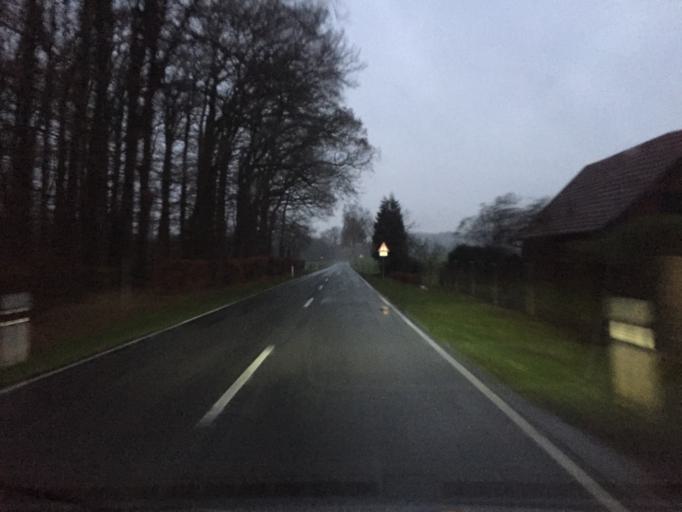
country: DE
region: Lower Saxony
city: Sudwalde
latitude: 52.8162
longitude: 8.8418
